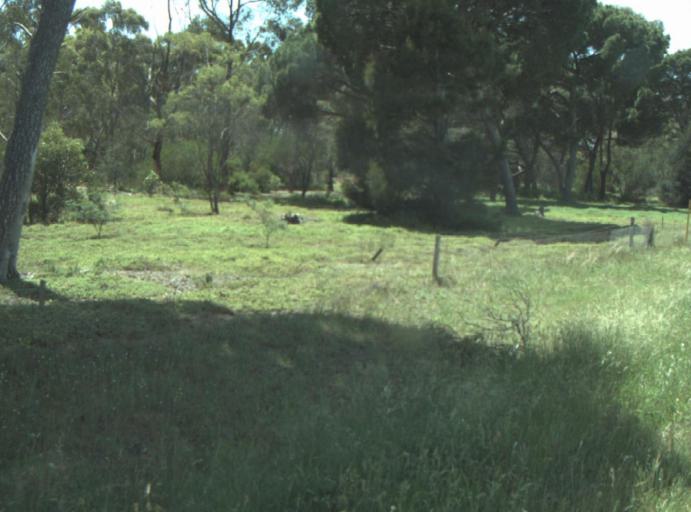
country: AU
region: Victoria
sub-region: Greater Geelong
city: Lara
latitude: -38.0095
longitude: 144.4059
